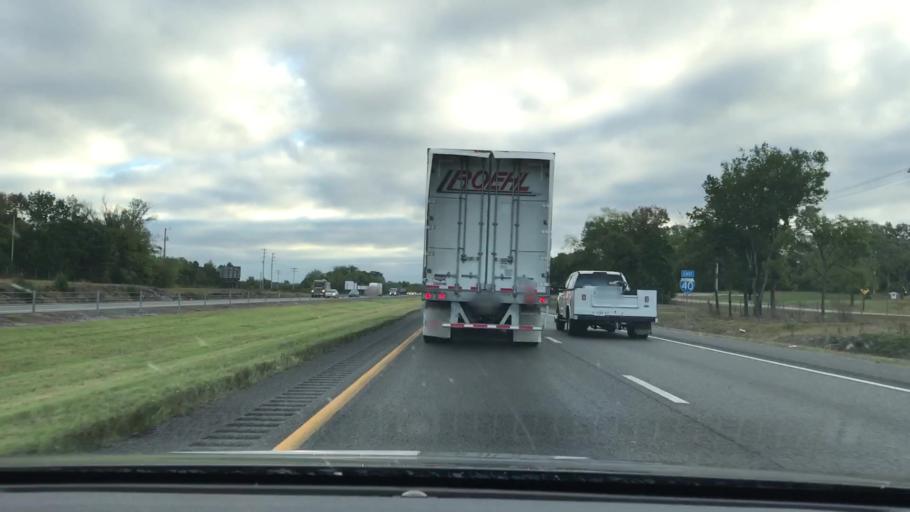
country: US
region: Tennessee
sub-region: Wilson County
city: Lebanon
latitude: 36.1826
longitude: -86.2918
